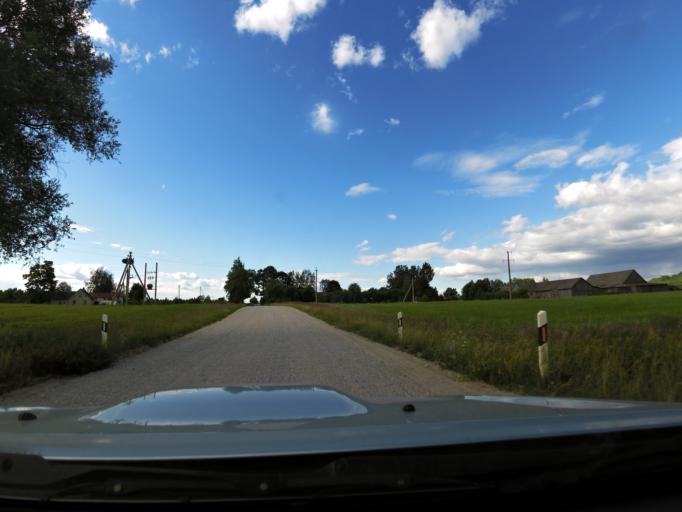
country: LT
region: Panevezys
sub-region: Birzai
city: Birzai
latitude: 56.1868
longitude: 24.9367
